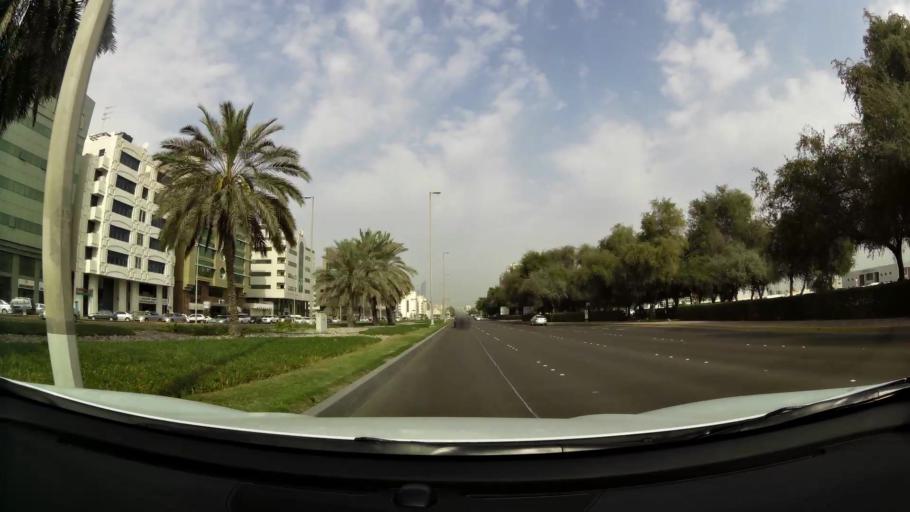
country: AE
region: Abu Dhabi
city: Abu Dhabi
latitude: 24.4594
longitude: 54.3891
